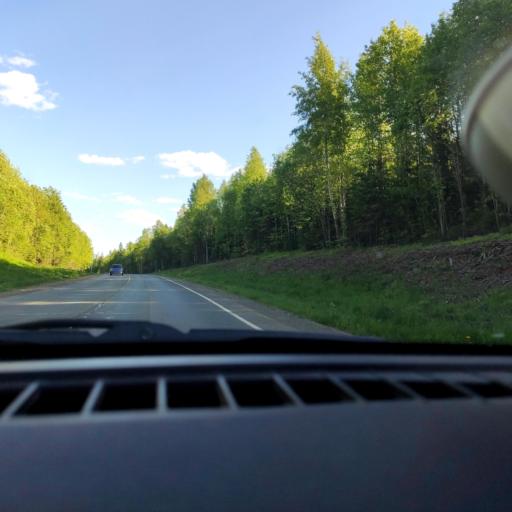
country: RU
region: Perm
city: Perm
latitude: 58.2251
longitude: 56.1642
